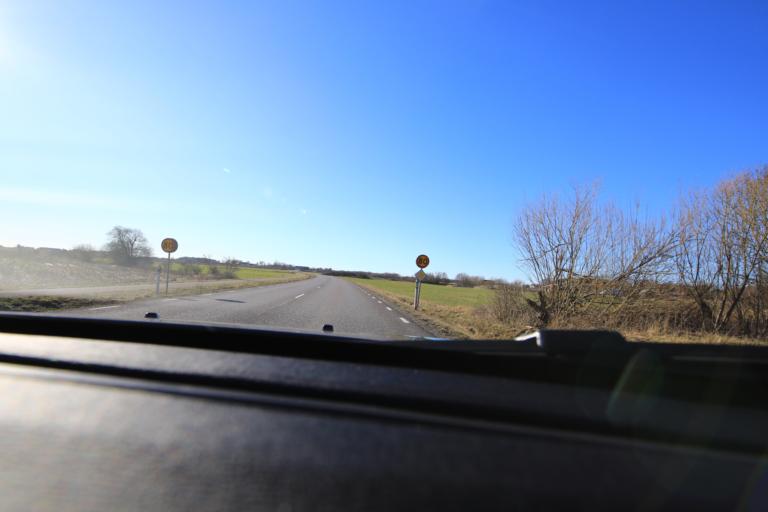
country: SE
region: Halland
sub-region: Varbergs Kommun
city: Tvaaker
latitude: 57.0485
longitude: 12.3458
